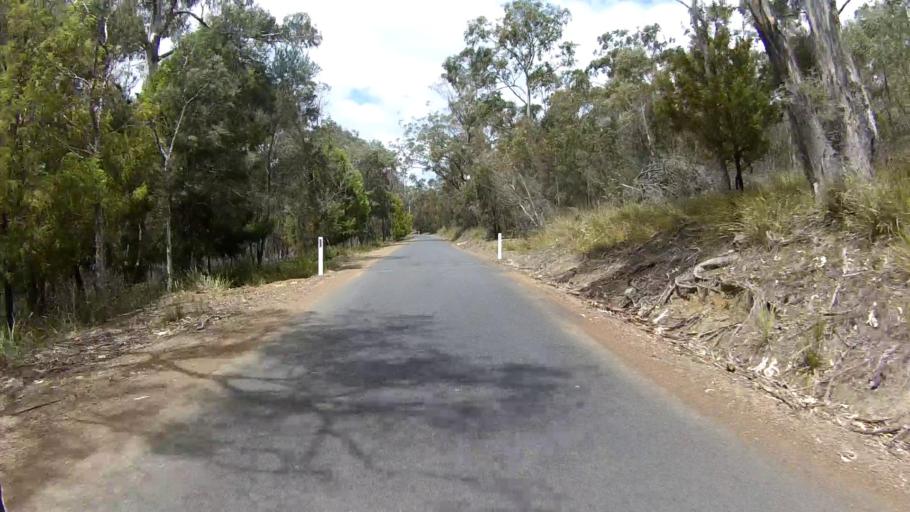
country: AU
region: Tasmania
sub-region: Sorell
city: Sorell
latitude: -42.5954
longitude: 147.9182
